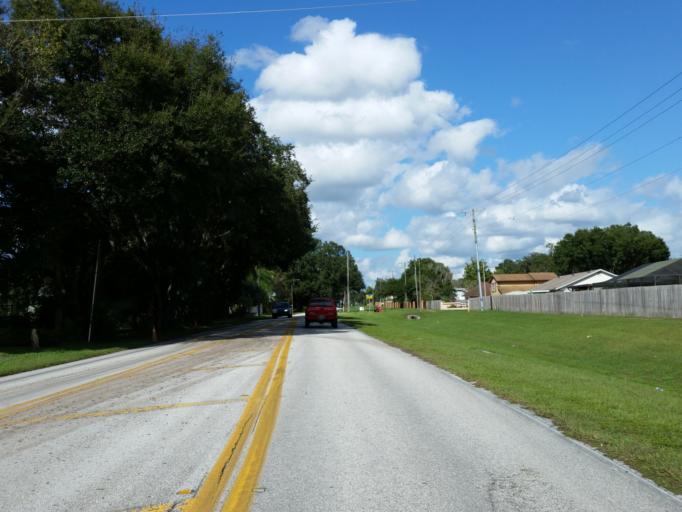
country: US
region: Florida
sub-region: Hillsborough County
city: Bloomingdale
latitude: 27.8998
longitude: -82.2774
